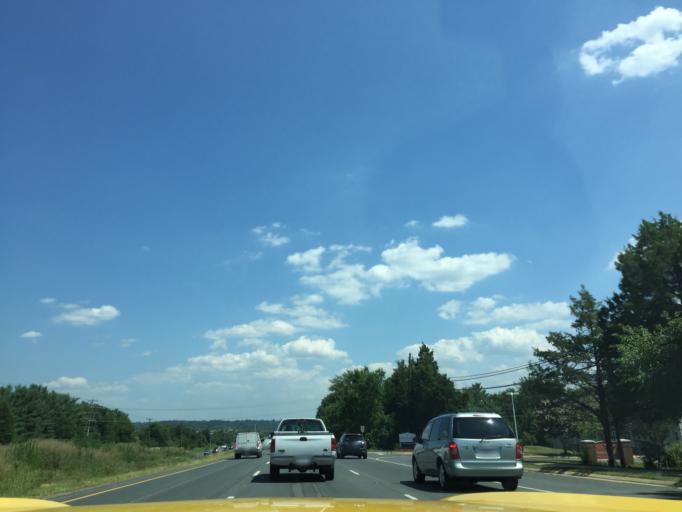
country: US
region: Virginia
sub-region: Loudoun County
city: Sugarland Run
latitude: 39.0239
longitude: -77.3895
